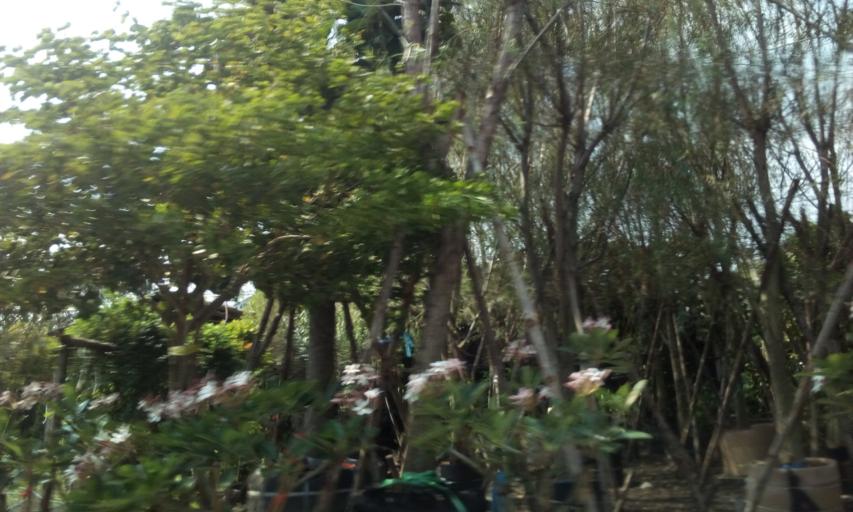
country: TH
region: Nakhon Nayok
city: Ongkharak
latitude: 14.1103
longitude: 100.9435
